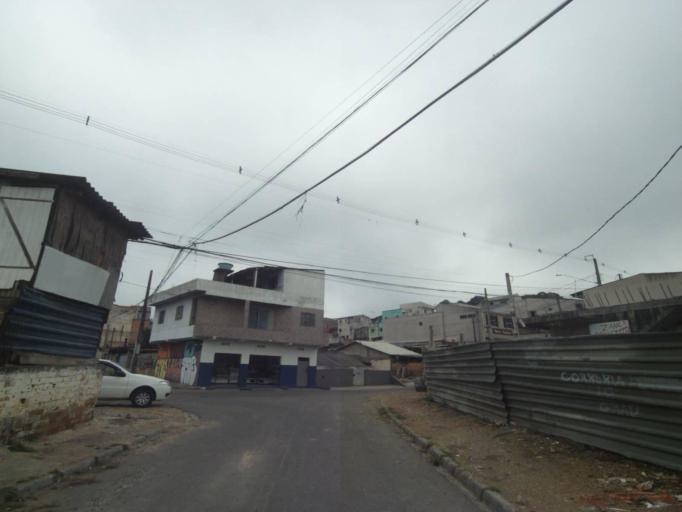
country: BR
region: Parana
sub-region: Curitiba
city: Curitiba
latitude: -25.4997
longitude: -49.3518
